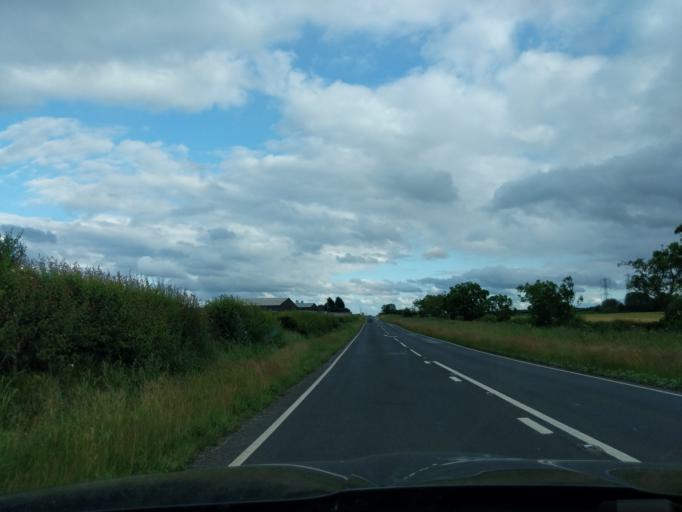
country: GB
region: England
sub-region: Northumberland
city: Seghill
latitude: 55.0909
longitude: -1.5535
